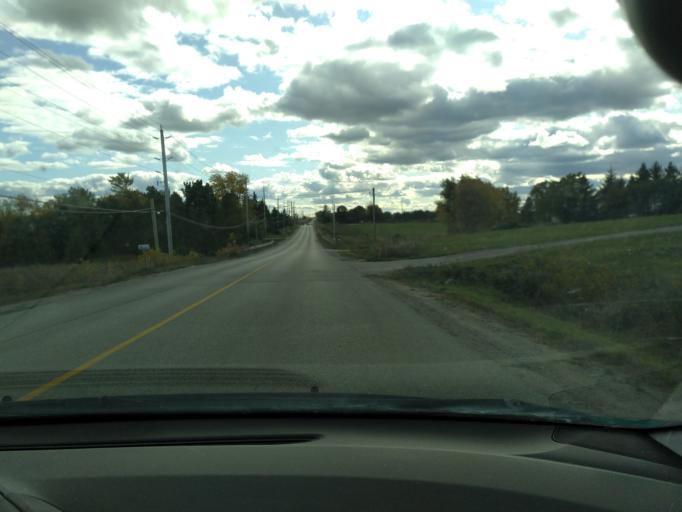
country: CA
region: Ontario
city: Bradford West Gwillimbury
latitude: 44.0973
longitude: -79.5996
